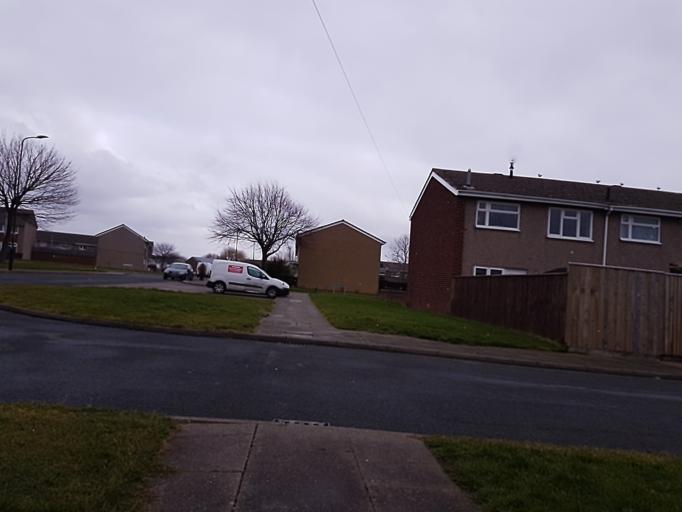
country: GB
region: England
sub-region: North East Lincolnshire
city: Great Coates
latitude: 53.5683
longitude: -0.1221
